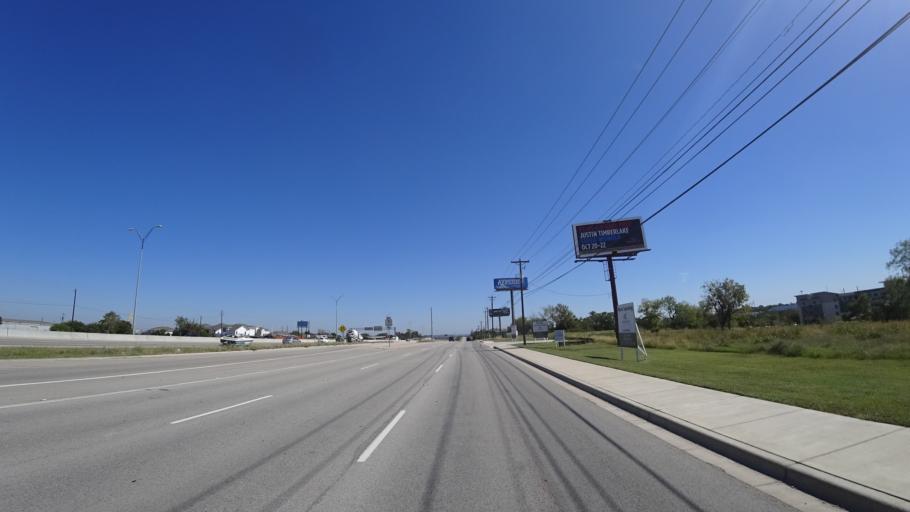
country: US
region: Texas
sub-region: Travis County
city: Austin
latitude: 30.2147
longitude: -97.7009
